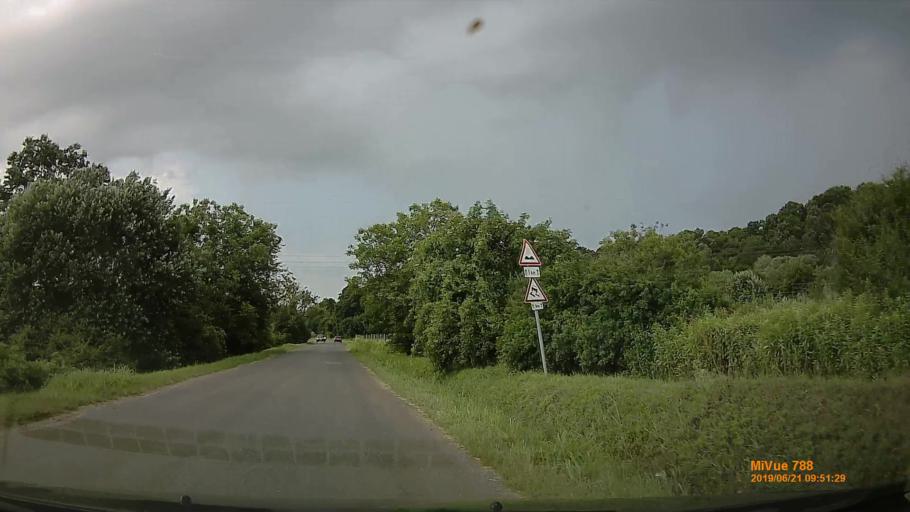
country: HU
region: Baranya
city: Sasd
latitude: 46.2515
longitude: 18.0219
